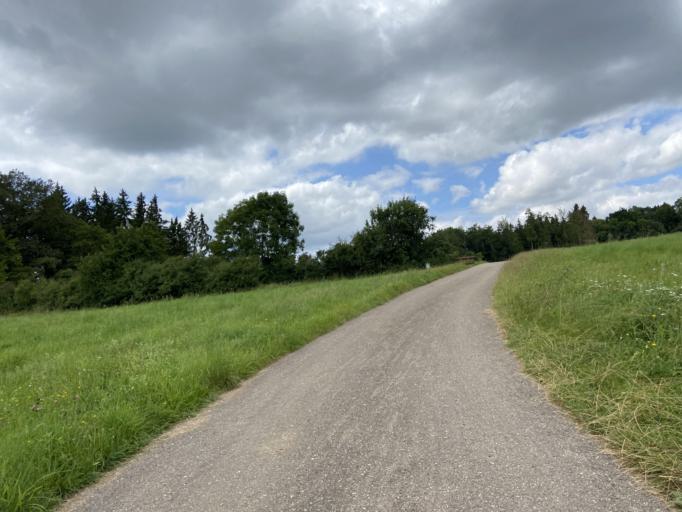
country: DE
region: Baden-Wuerttemberg
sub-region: Tuebingen Region
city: Bingen
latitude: 48.0972
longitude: 9.2904
